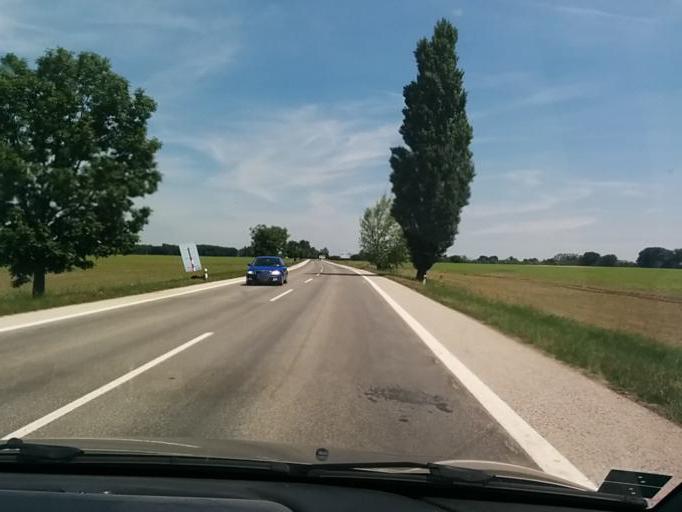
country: SK
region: Trnavsky
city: Sladkovicovo
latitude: 48.2204
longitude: 17.6643
